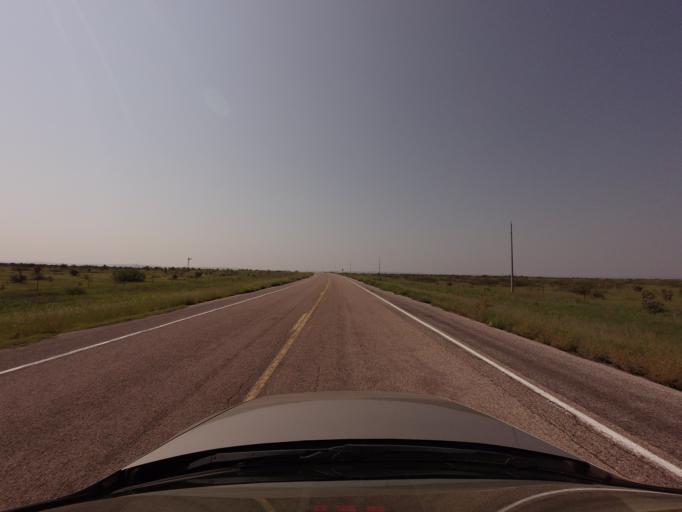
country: US
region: New Mexico
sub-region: Quay County
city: Tucumcari
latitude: 34.9506
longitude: -103.7596
